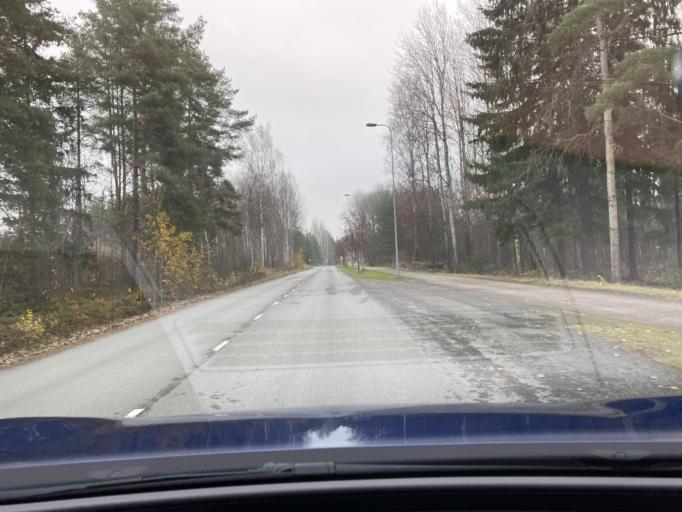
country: FI
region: Pirkanmaa
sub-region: Tampere
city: Nokia
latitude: 61.4635
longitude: 23.5069
